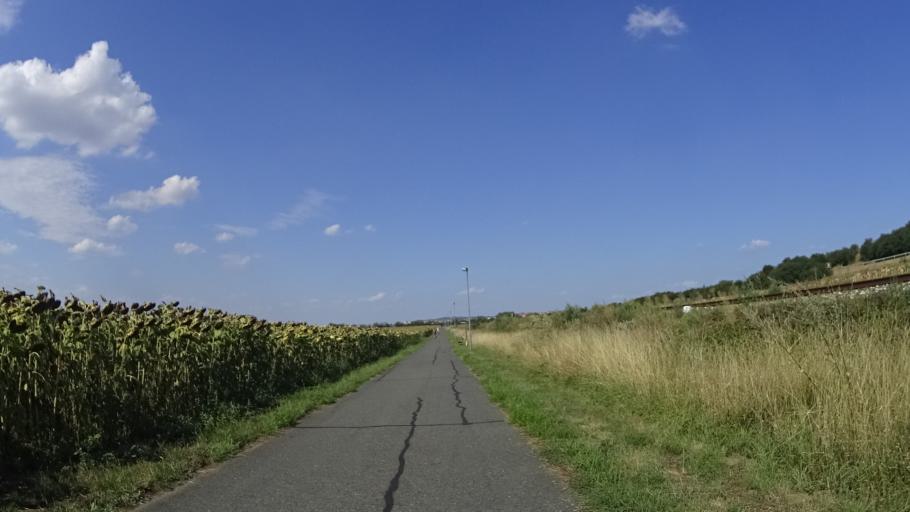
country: CZ
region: Zlin
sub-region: Okres Zlin
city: Ostrozska Nova Ves
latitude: 49.0227
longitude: 17.4503
